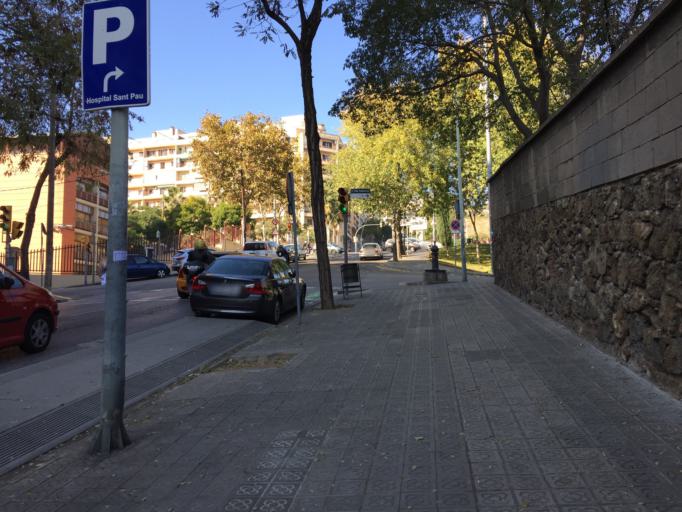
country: ES
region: Catalonia
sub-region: Provincia de Barcelona
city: Horta-Guinardo
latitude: 41.4134
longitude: 2.1716
